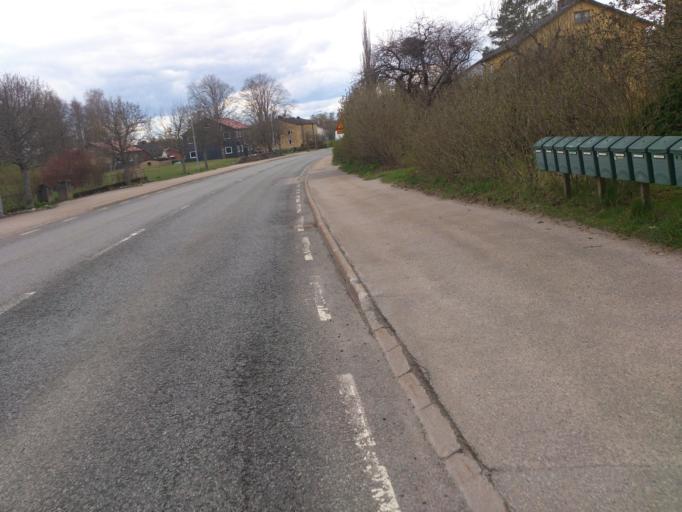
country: SE
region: Vaestra Goetaland
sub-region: Falkopings Kommun
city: Falkoeping
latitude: 57.9869
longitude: 13.5385
